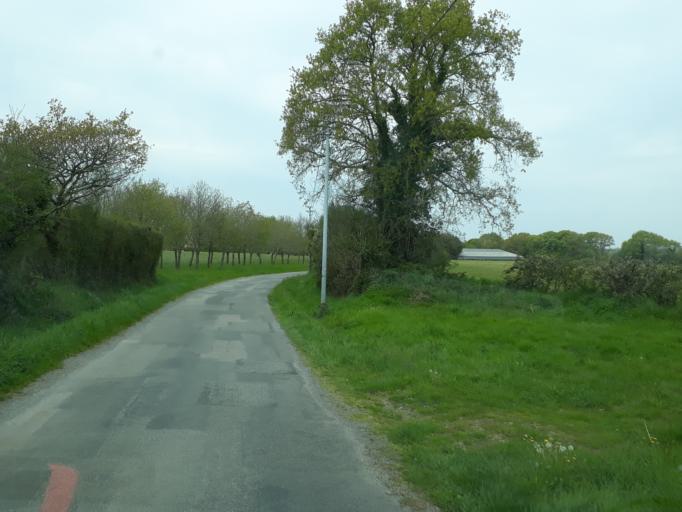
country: FR
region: Brittany
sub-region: Departement du Morbihan
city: Theix
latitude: 47.6007
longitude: -2.6834
